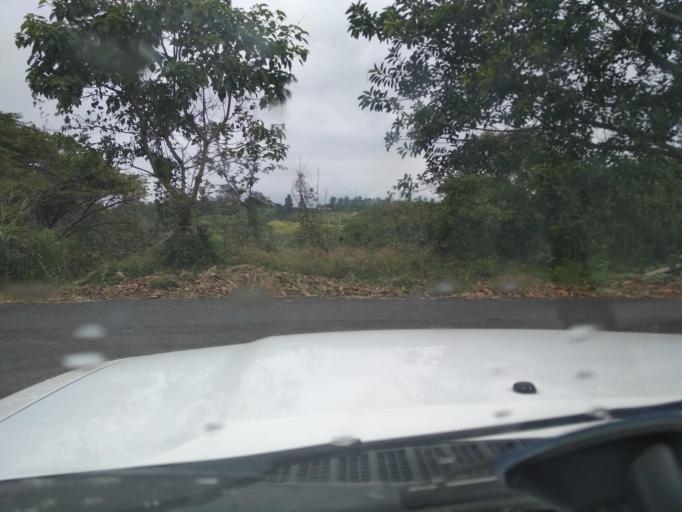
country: MX
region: Veracruz
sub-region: Emiliano Zapata
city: Dos Rios
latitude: 19.5340
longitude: -96.8101
